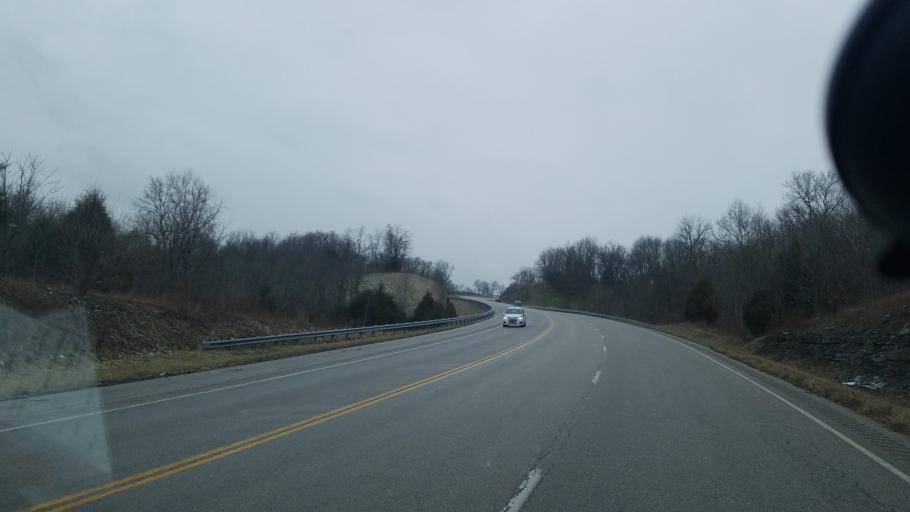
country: US
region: Kentucky
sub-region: Bath County
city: Owingsville
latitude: 38.2746
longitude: -83.8170
